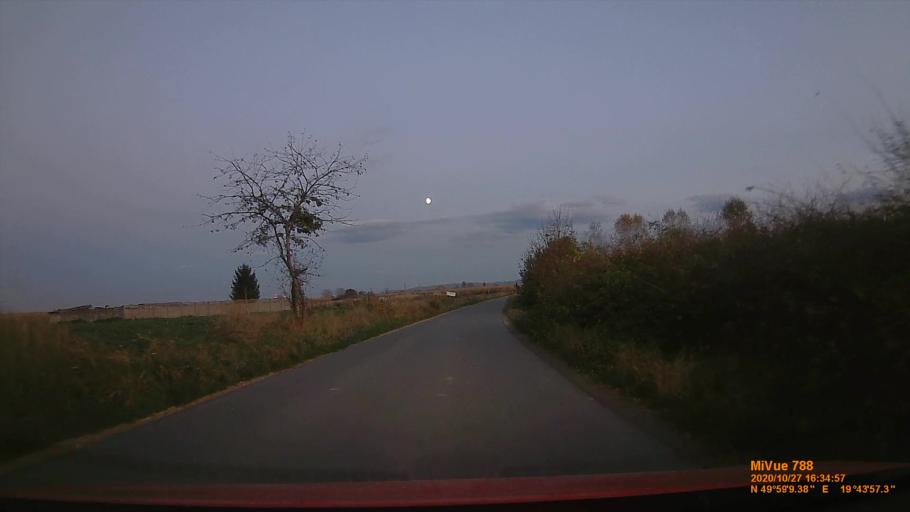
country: PL
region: Lesser Poland Voivodeship
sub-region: Powiat krakowski
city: Wolowice
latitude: 49.9859
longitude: 19.7326
